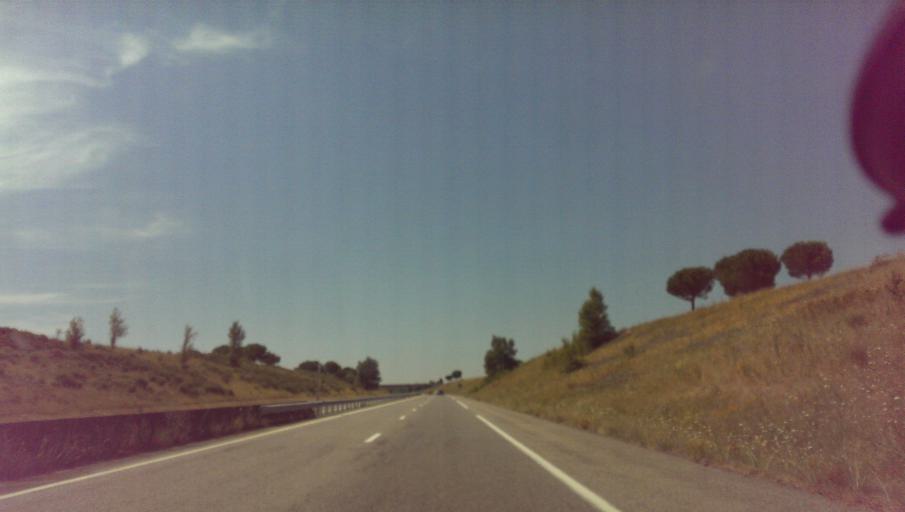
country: FR
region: Midi-Pyrenees
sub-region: Departement de la Haute-Garonne
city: Villenouvelle
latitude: 43.4052
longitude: 1.6460
